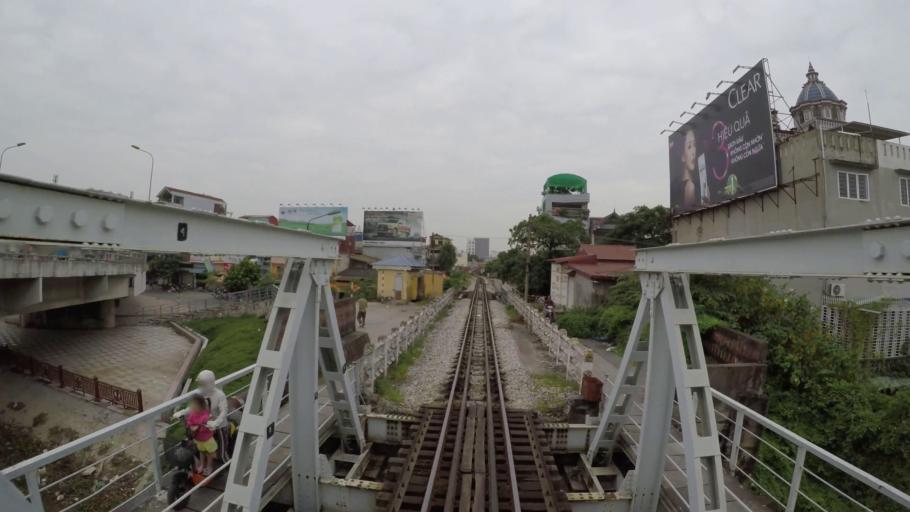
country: VN
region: Hai Phong
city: Haiphong
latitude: 20.8707
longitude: 106.6519
